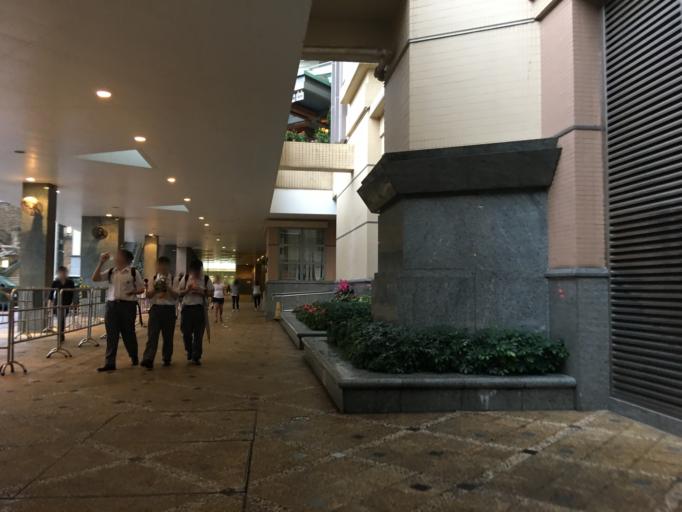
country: HK
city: Tai O
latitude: 22.2915
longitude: 113.9476
